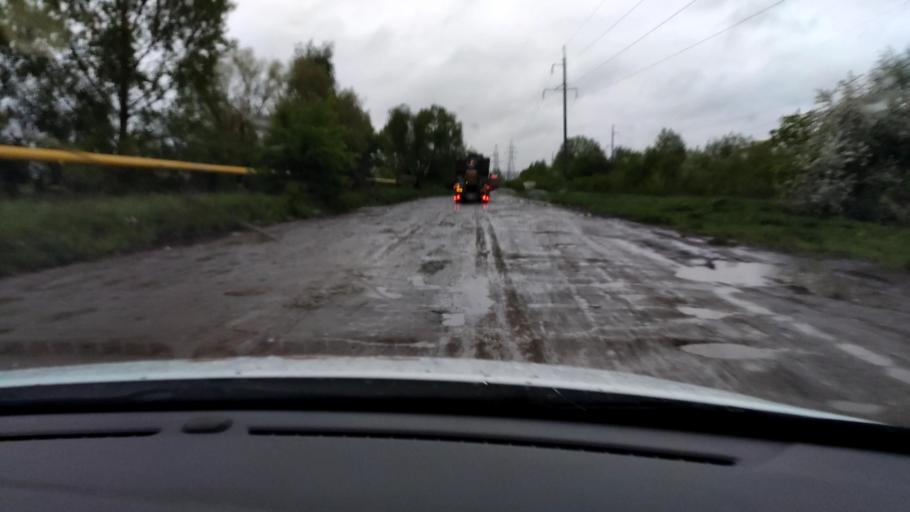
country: RU
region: Tatarstan
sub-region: Gorod Kazan'
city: Kazan
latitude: 55.7226
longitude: 49.1253
